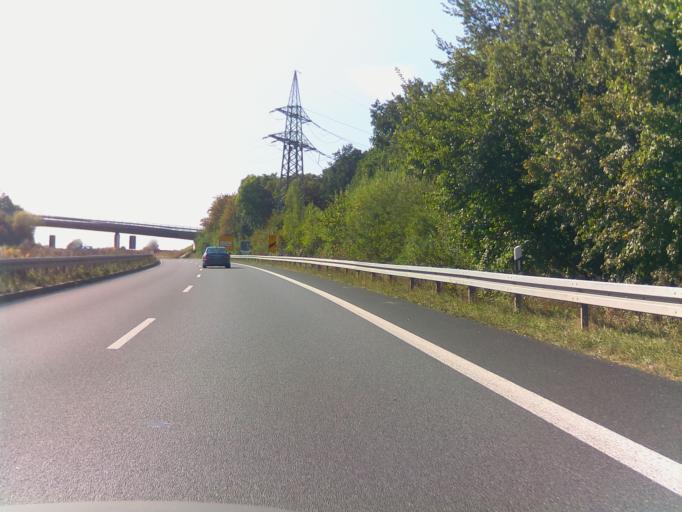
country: DE
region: Bavaria
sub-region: Upper Franconia
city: Michelau
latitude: 50.1517
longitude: 11.0911
